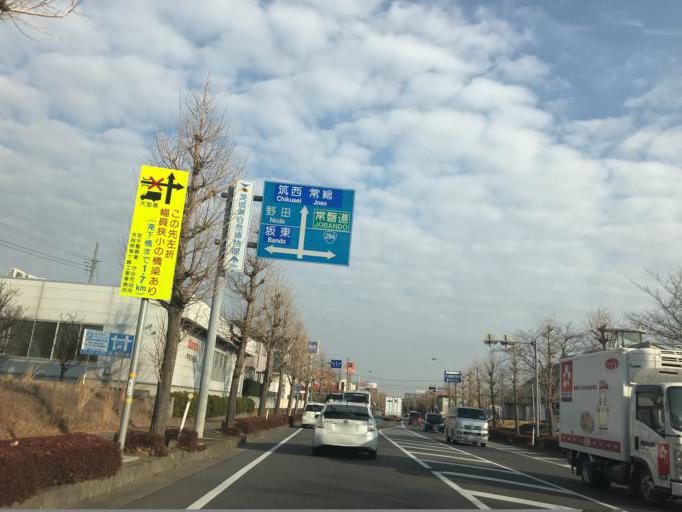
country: JP
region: Ibaraki
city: Moriya
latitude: 35.9658
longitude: 139.9710
